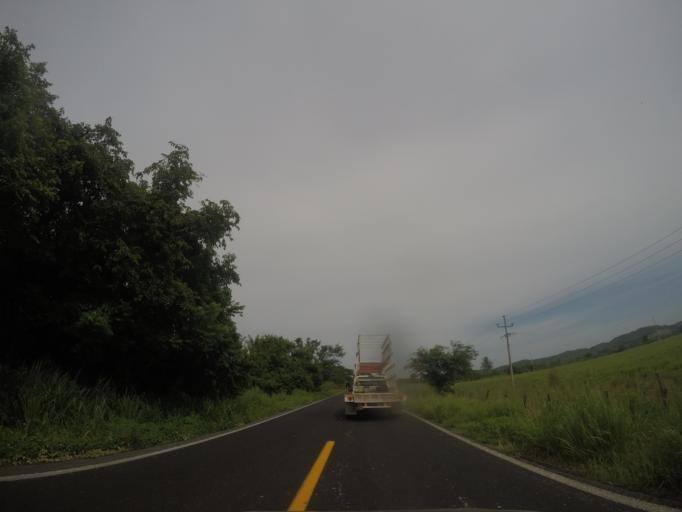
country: MX
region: Oaxaca
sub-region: Villa de Tututepec de Melchor Ocampo
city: Santa Rosa de Lima
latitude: 16.0221
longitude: -97.5531
